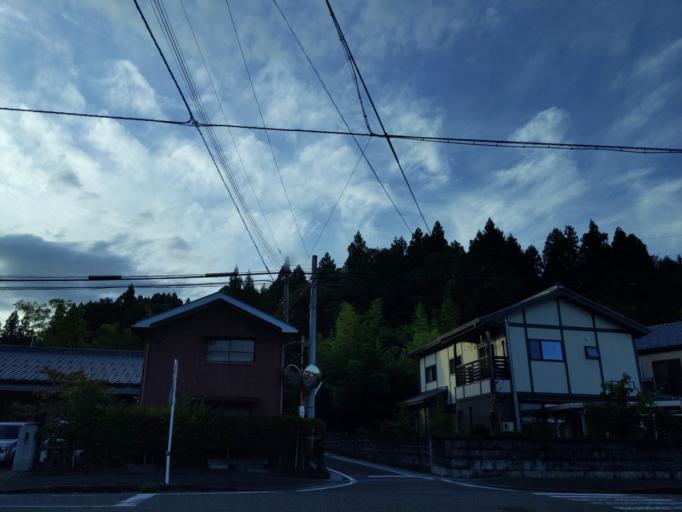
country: JP
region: Niigata
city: Kashiwazaki
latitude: 37.4396
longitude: 138.6280
